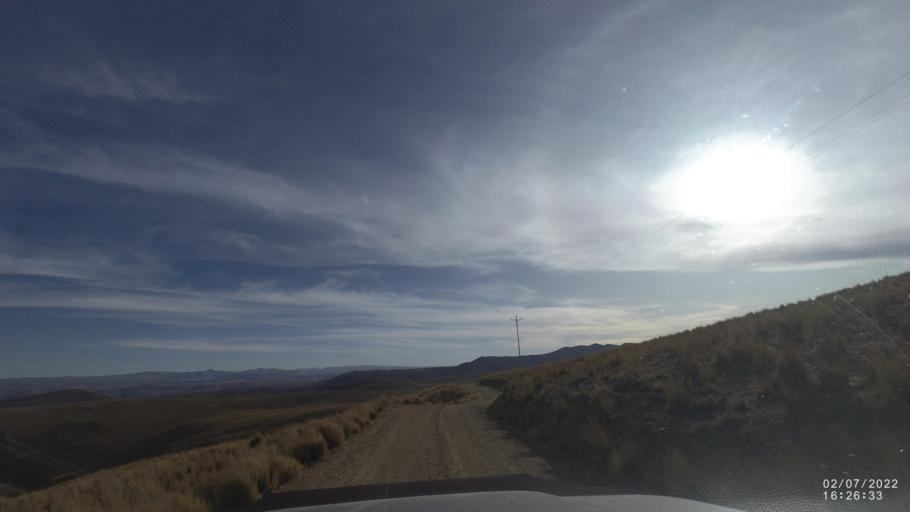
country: BO
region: Cochabamba
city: Irpa Irpa
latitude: -17.9474
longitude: -66.4664
